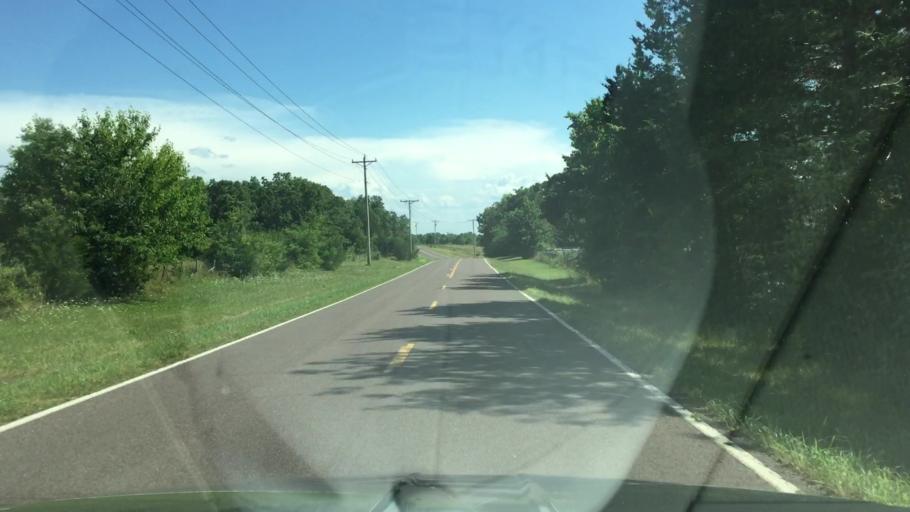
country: US
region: Missouri
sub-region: Miller County
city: Tuscumbia
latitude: 38.1107
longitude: -92.4727
